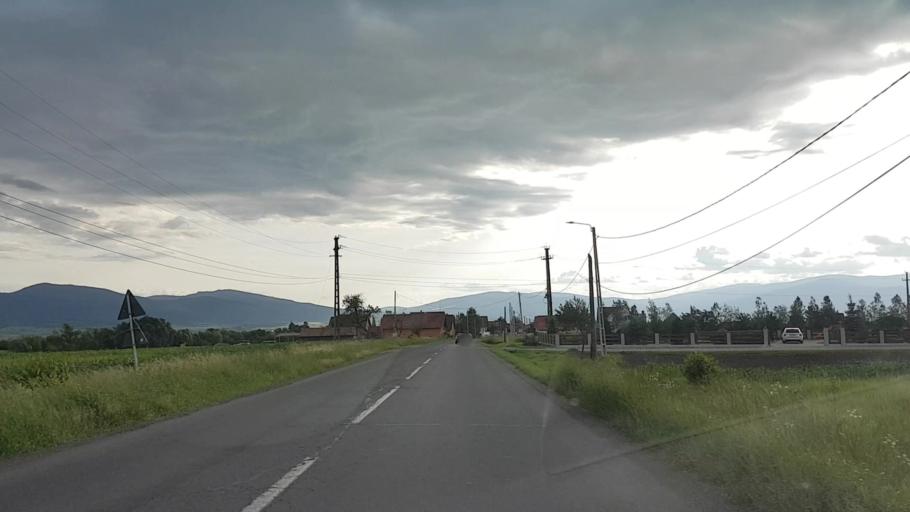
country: RO
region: Harghita
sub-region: Comuna Ciumani
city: Ciumani
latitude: 46.7070
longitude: 25.5300
